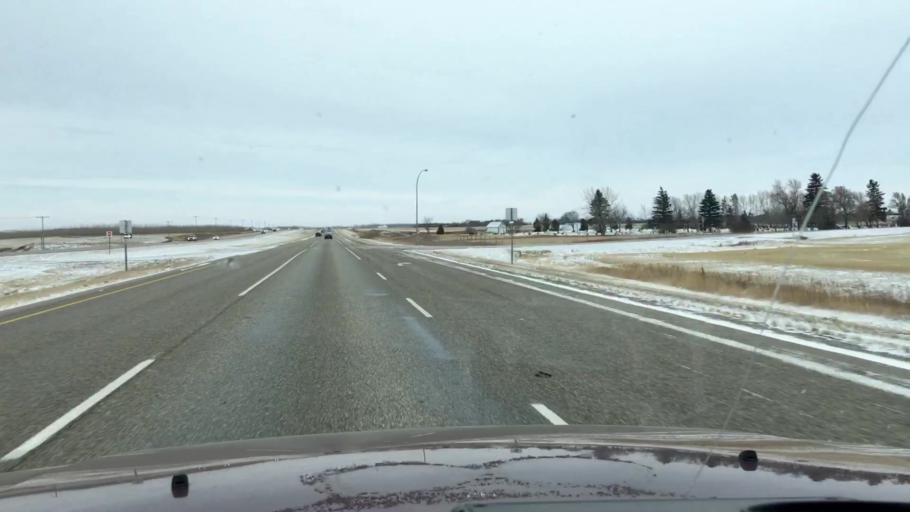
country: CA
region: Saskatchewan
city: Watrous
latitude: 51.0609
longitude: -105.8233
